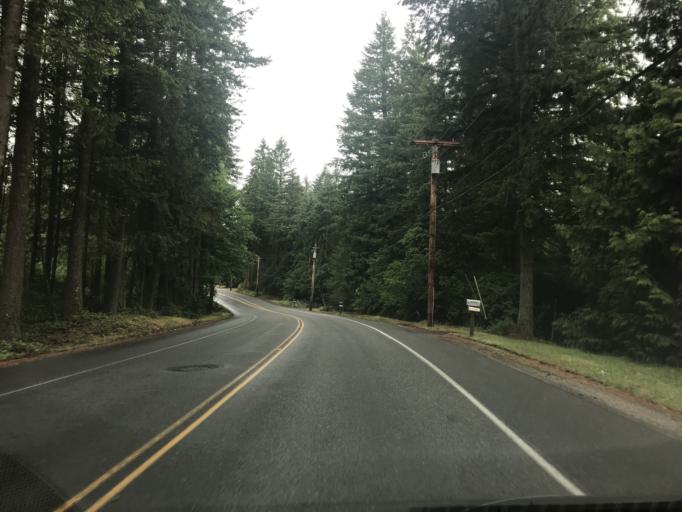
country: US
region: Washington
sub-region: King County
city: Lake Morton-Berrydale
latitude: 47.3424
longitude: -122.0695
